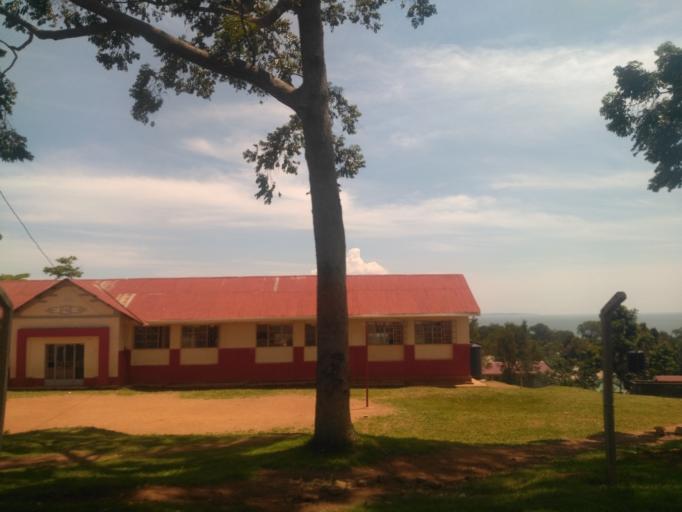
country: UG
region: Central Region
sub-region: Wakiso District
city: Entebbe
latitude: 0.0439
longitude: 32.4653
